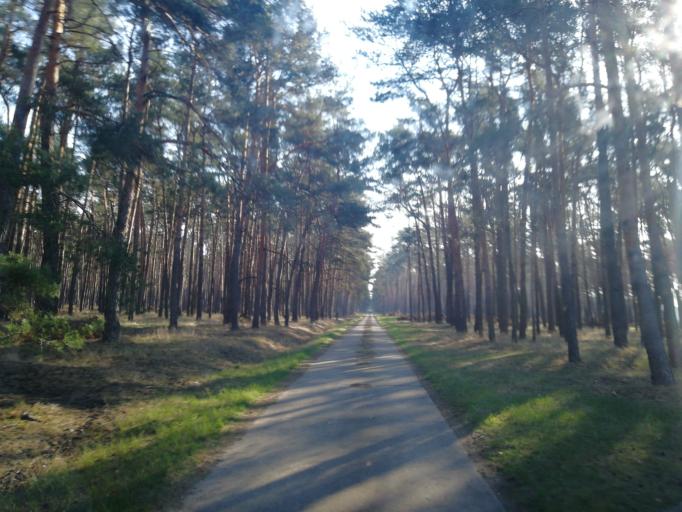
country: DE
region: Brandenburg
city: Drahnsdorf
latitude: 51.8884
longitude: 13.5334
